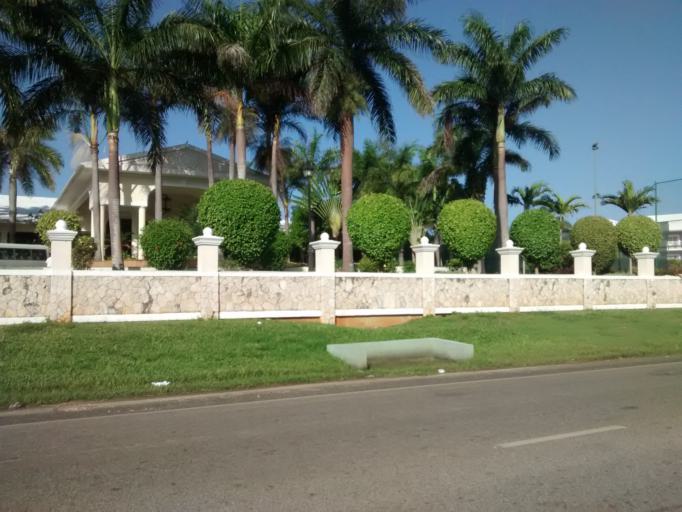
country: JM
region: Westmoreland
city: Negril
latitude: 18.3557
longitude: -78.3358
